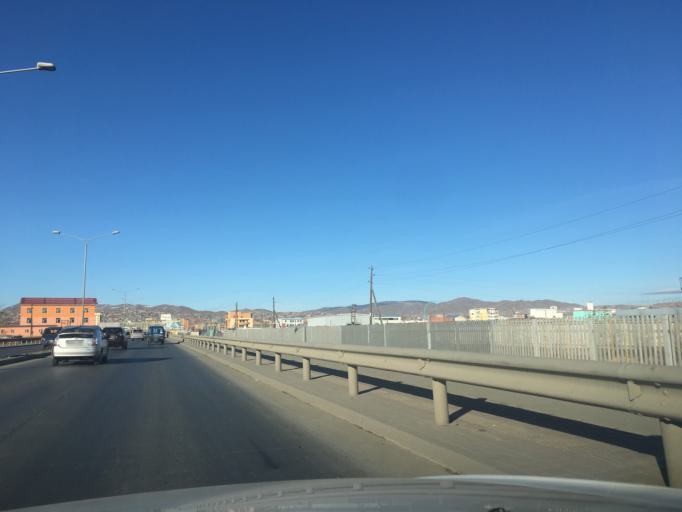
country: MN
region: Ulaanbaatar
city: Ulaanbaatar
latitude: 47.9029
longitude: 106.7858
